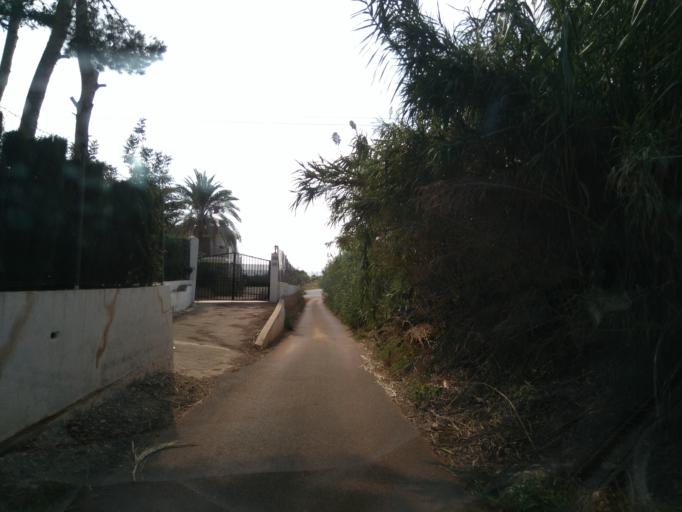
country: ES
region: Valencia
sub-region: Provincia de Valencia
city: Masalaves
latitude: 39.1728
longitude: -0.5529
